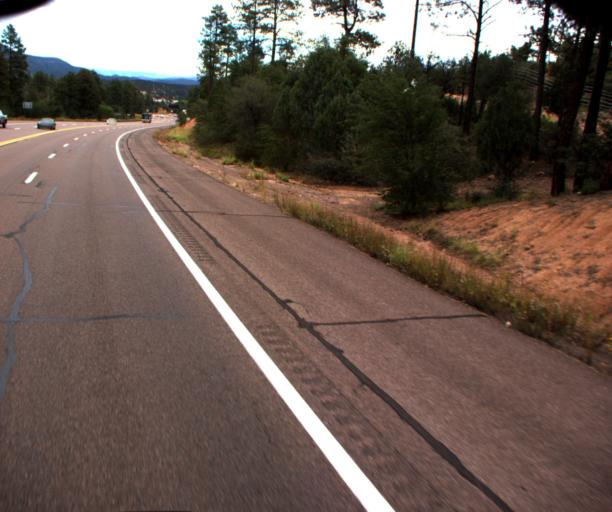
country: US
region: Arizona
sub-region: Gila County
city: Sun Valley
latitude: 34.2513
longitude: -111.2764
